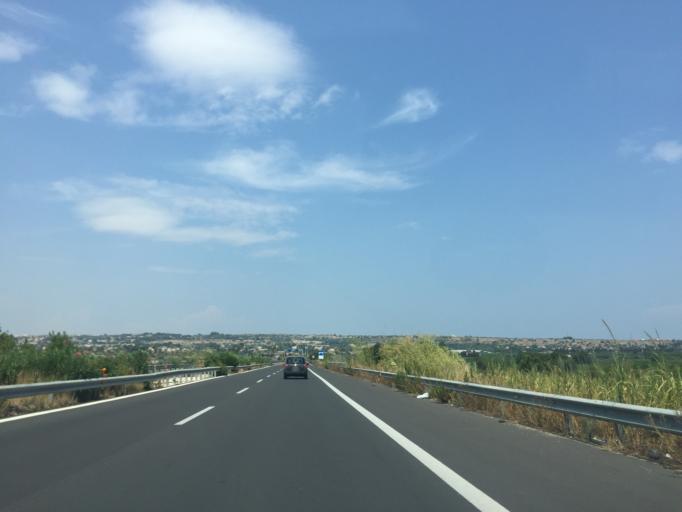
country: IT
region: Sicily
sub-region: Provincia di Siracusa
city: Belvedere
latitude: 37.0644
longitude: 15.2261
